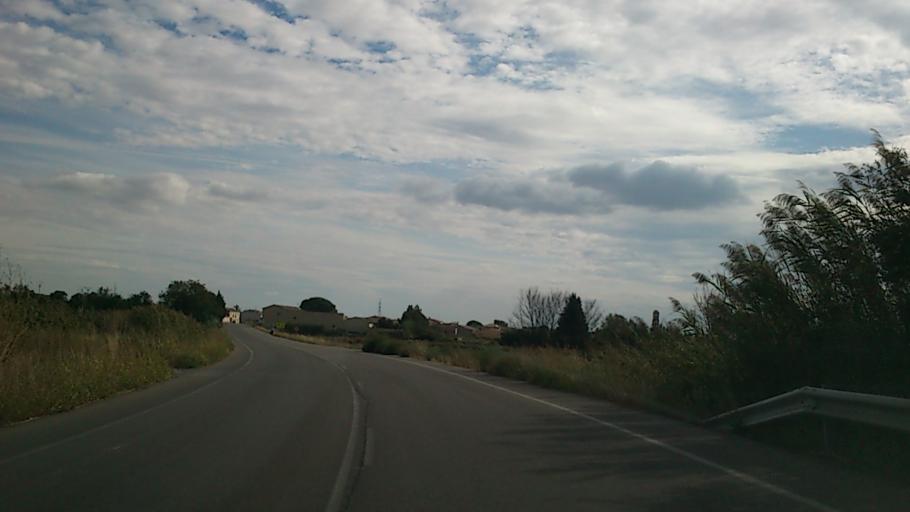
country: ES
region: Aragon
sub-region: Provincia de Zaragoza
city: Villanueva de Gallego
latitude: 41.7666
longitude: -0.7960
